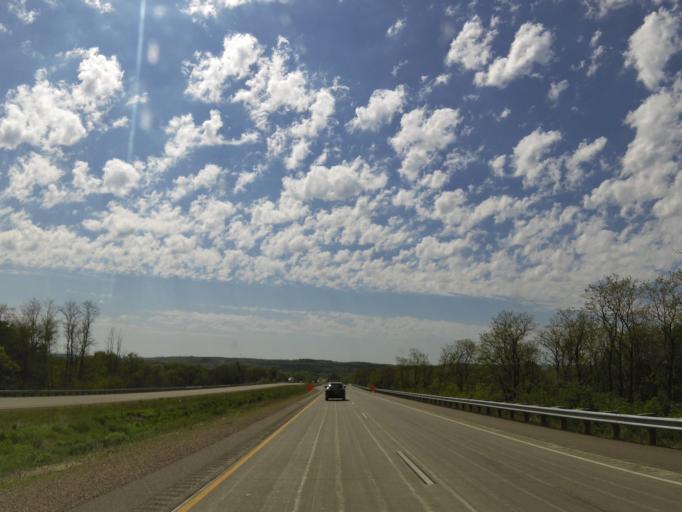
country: US
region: Wisconsin
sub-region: Eau Claire County
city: Eau Claire
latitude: 44.7954
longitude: -91.5512
